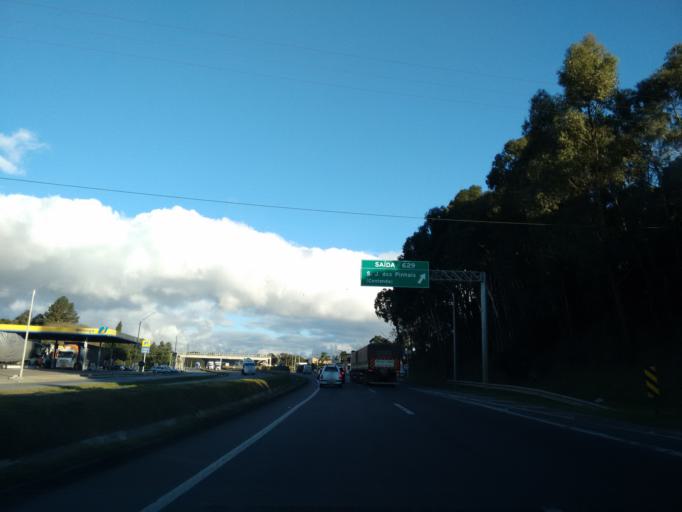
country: BR
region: Parana
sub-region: Sao Jose Dos Pinhais
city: Sao Jose dos Pinhais
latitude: -25.6964
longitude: -49.1447
